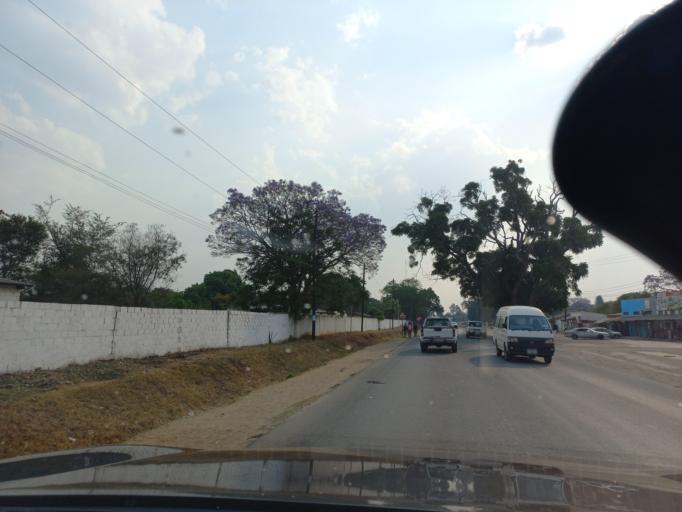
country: ZM
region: Lusaka
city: Lusaka
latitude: -15.4623
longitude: 28.2463
